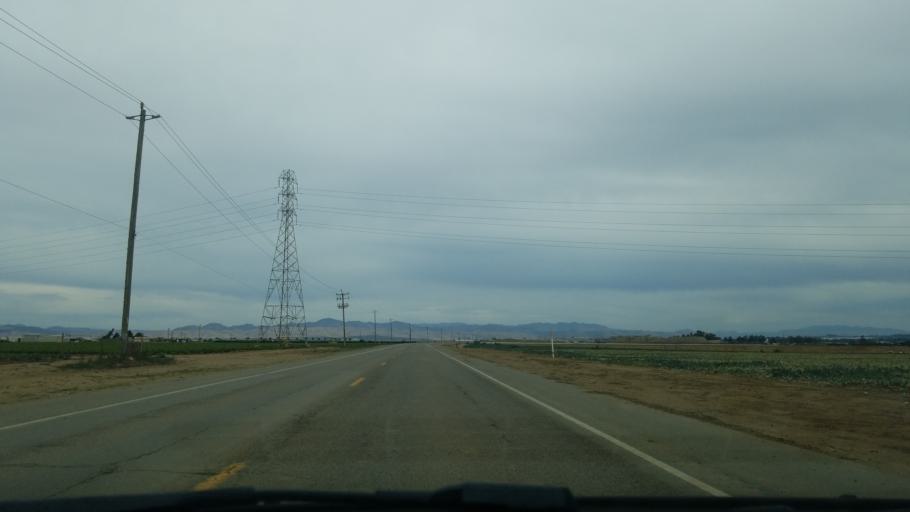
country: US
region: California
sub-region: Santa Barbara County
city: Santa Maria
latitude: 34.9198
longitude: -120.5041
